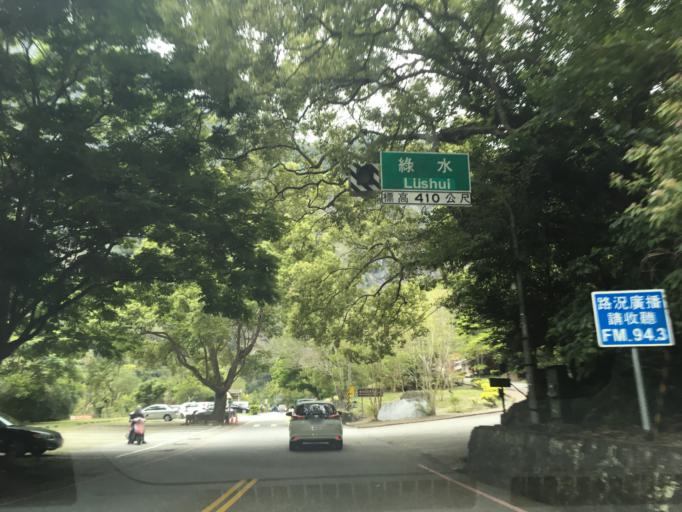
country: TW
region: Taiwan
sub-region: Hualien
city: Hualian
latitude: 24.1798
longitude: 121.5091
